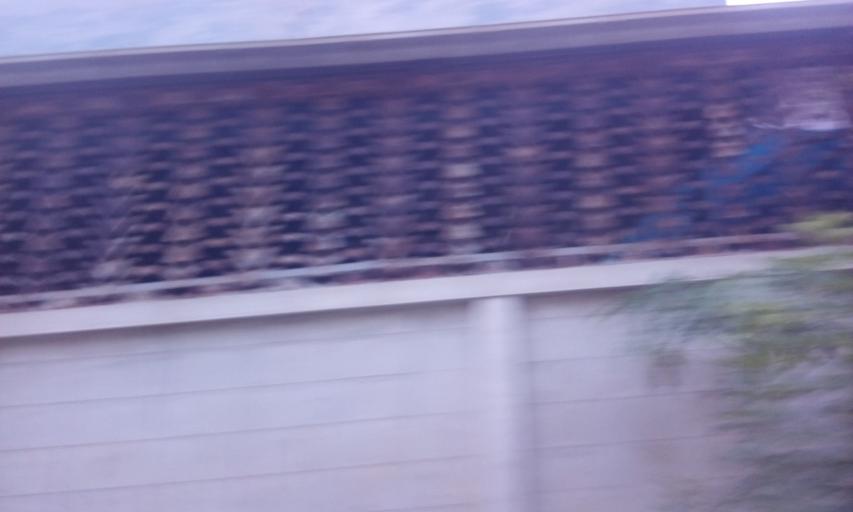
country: TH
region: Nonthaburi
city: Sai Noi
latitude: 13.9732
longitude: 100.3186
